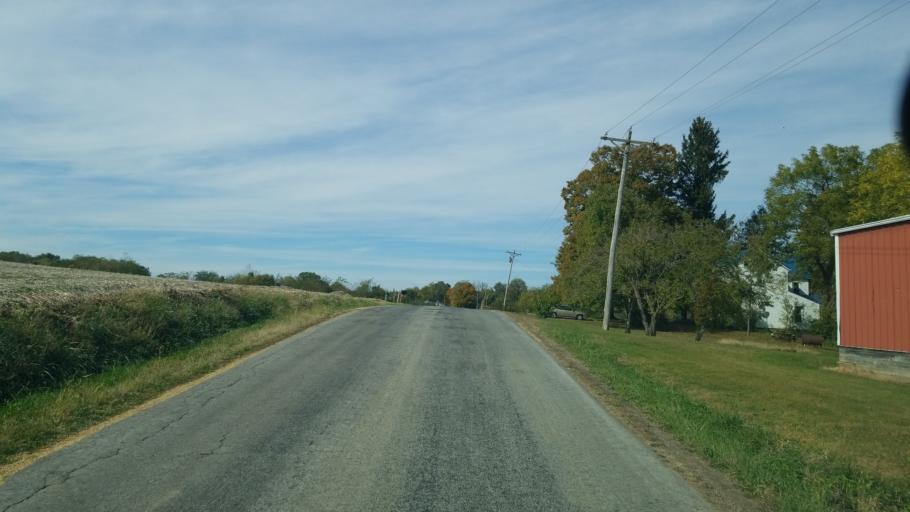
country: US
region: Ohio
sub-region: Highland County
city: Leesburg
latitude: 39.3175
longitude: -83.4693
